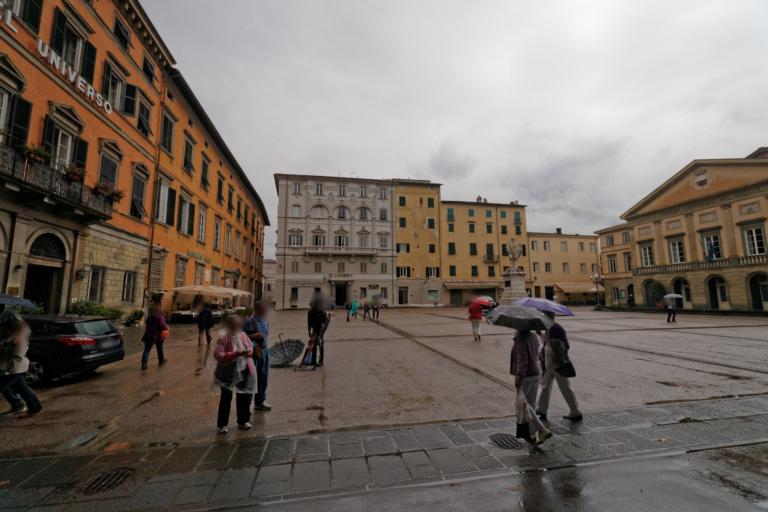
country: IT
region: Tuscany
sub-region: Provincia di Lucca
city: Lucca
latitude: 43.8410
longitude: 10.5028
